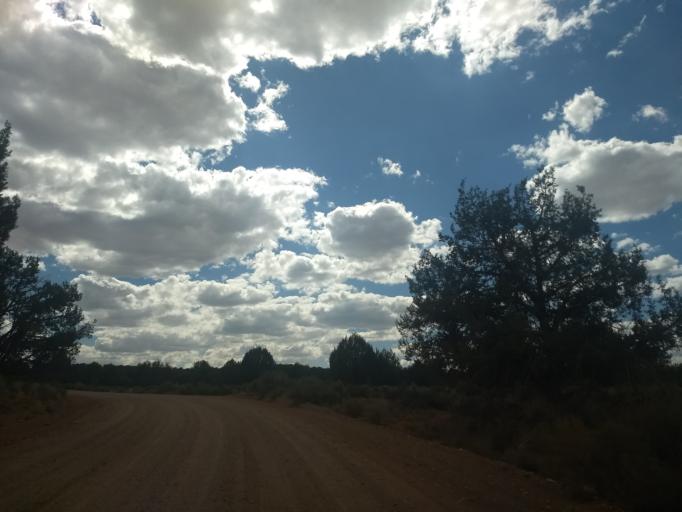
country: US
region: Utah
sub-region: Kane County
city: Kanab
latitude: 37.1518
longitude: -112.5439
